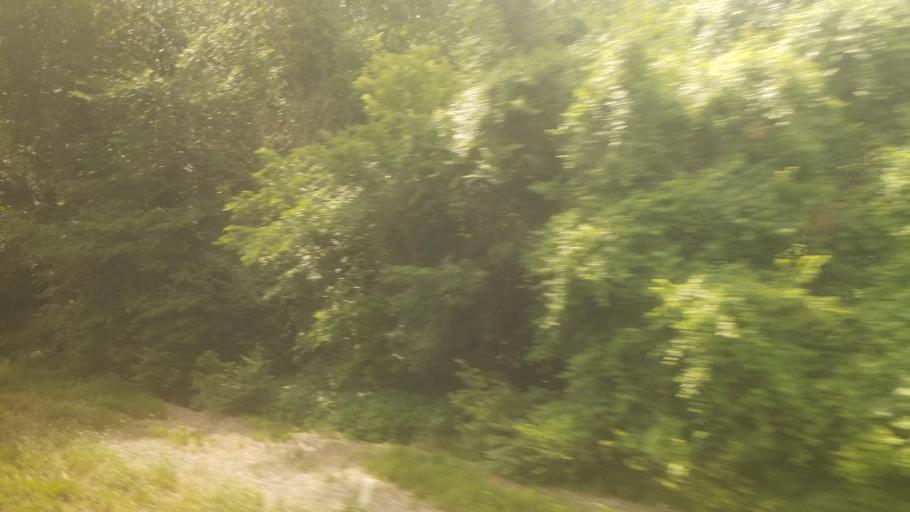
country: US
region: Missouri
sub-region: Jackson County
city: East Independence
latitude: 39.1565
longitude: -94.3812
